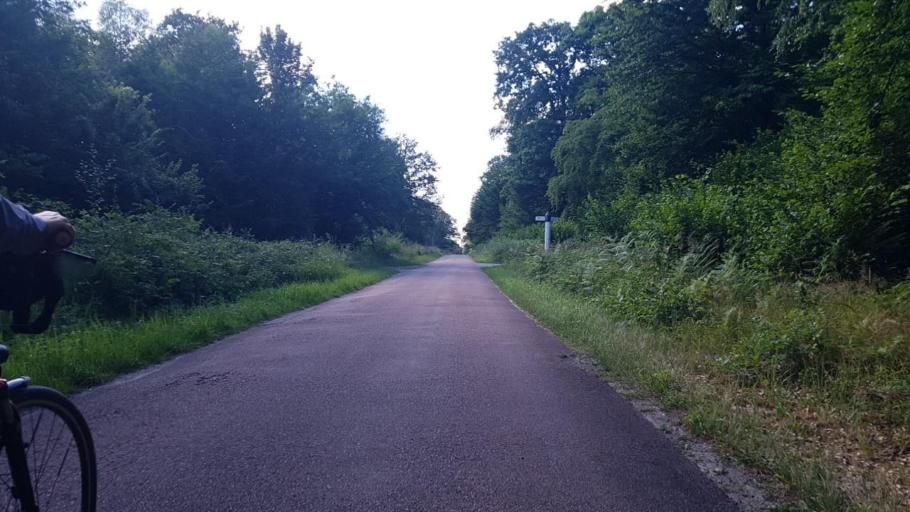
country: FR
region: Picardie
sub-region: Departement de l'Oise
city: Ver-sur-Launette
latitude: 49.1437
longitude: 2.6507
